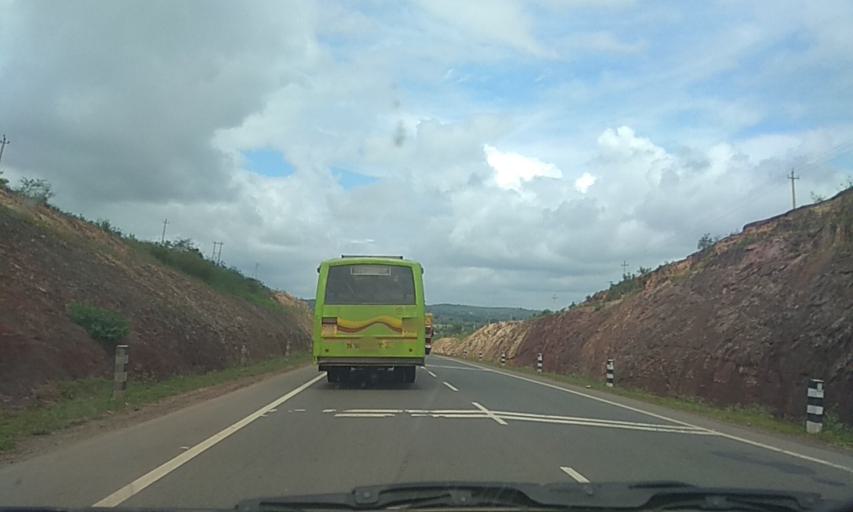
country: IN
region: Karnataka
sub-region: Dharwad
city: Hubli
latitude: 15.4020
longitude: 74.9961
